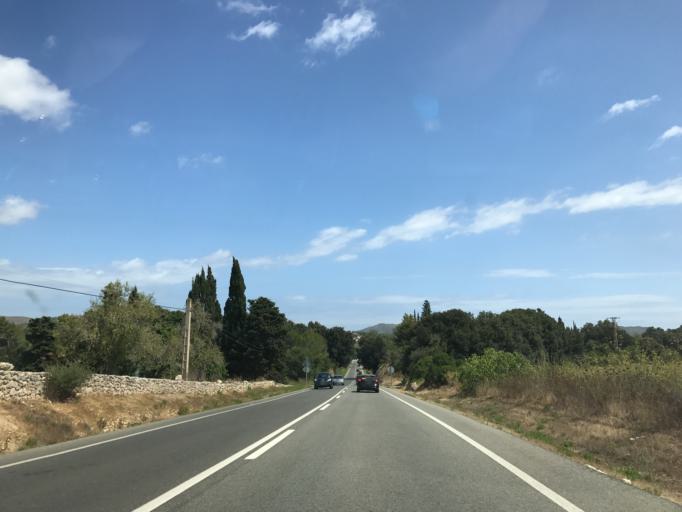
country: ES
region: Balearic Islands
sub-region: Illes Balears
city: Arta
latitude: 39.6815
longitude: 3.3417
